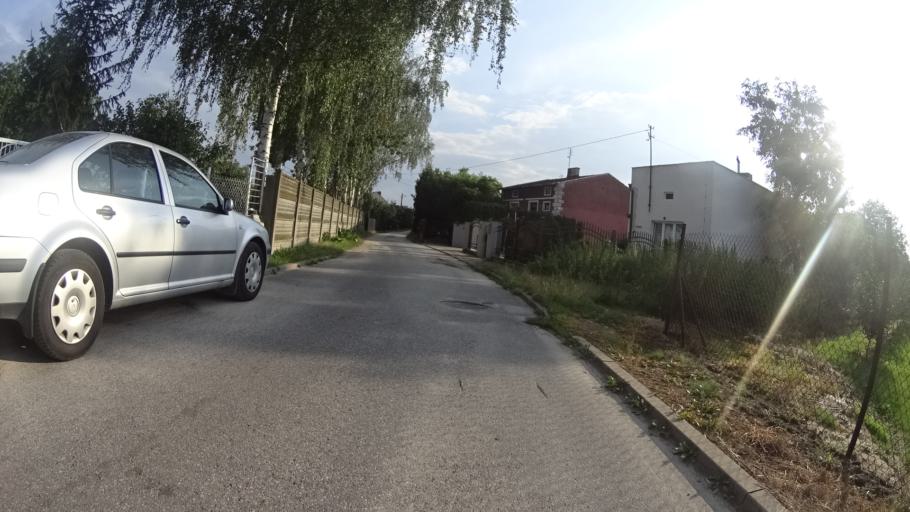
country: PL
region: Masovian Voivodeship
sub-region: Powiat grojecki
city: Mogielnica
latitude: 51.6892
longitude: 20.7258
